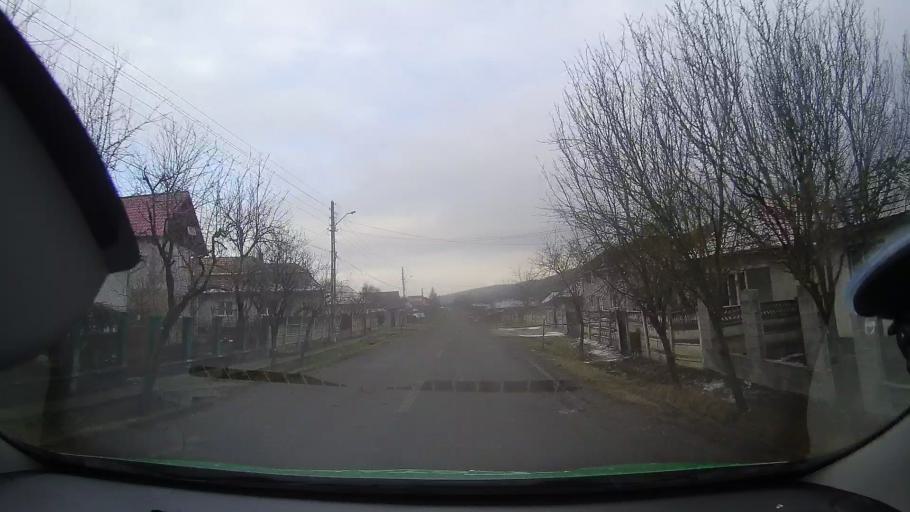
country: RO
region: Alba
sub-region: Comuna Farau
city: Farau
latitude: 46.3877
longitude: 24.0263
